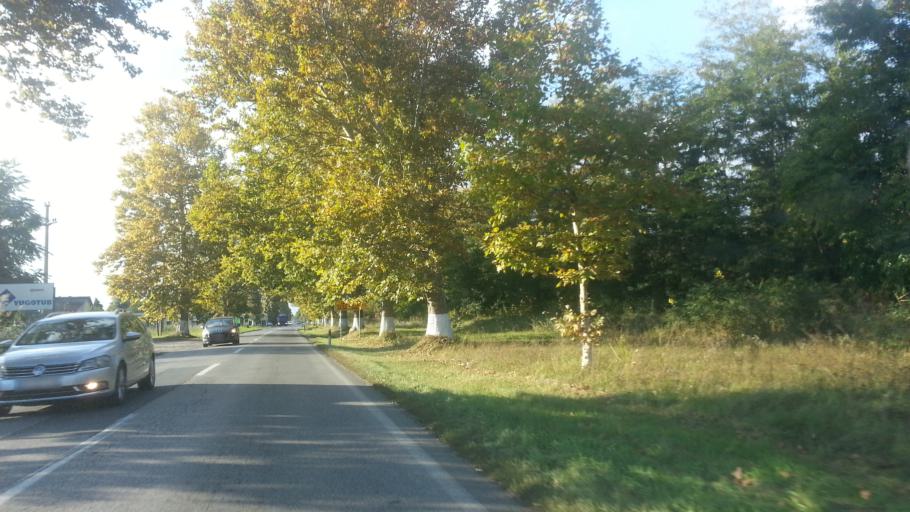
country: RS
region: Autonomna Pokrajina Vojvodina
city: Nova Pazova
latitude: 44.9363
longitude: 20.2309
